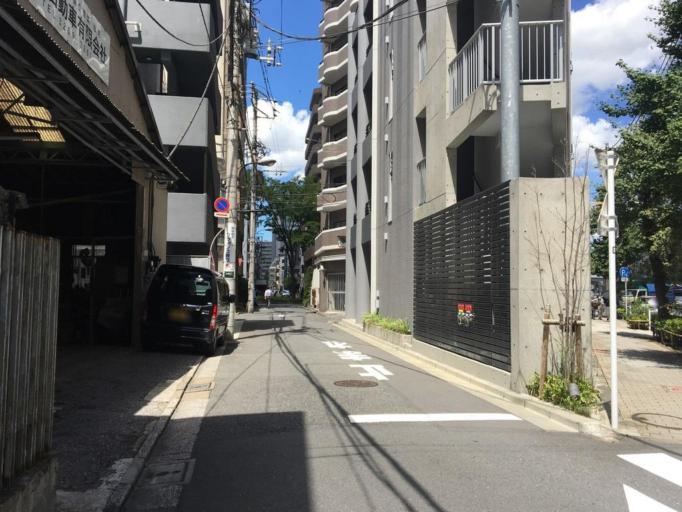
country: JP
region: Tokyo
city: Tokyo
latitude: 35.7068
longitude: 139.7312
